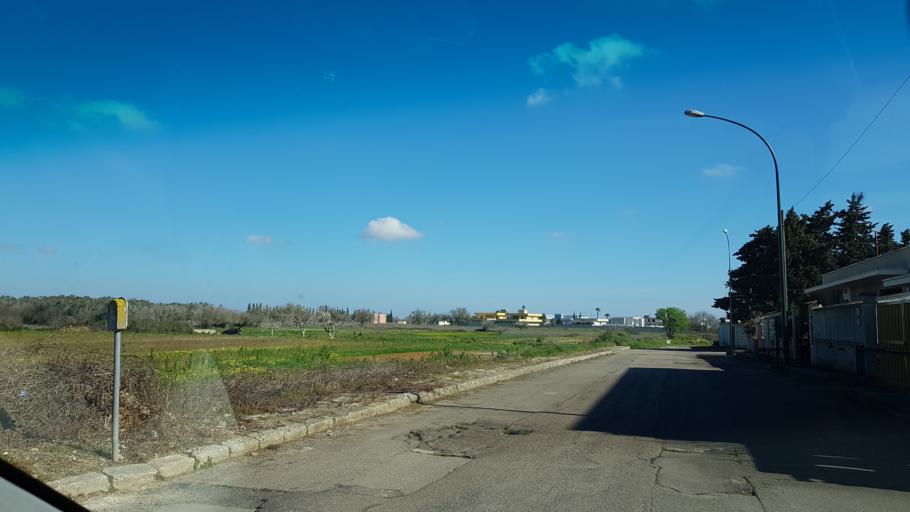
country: IT
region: Apulia
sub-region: Provincia di Lecce
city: Squinzano
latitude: 40.4370
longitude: 18.0499
